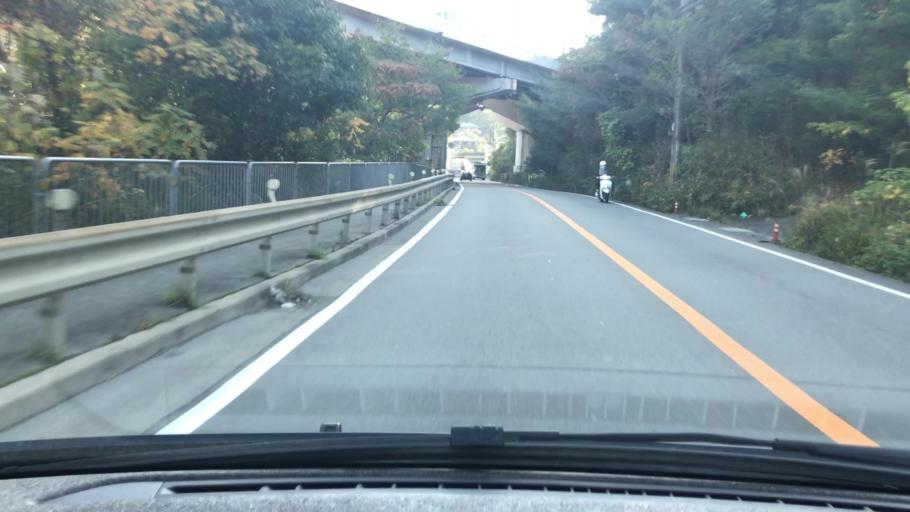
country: JP
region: Hyogo
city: Sandacho
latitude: 34.8338
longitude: 135.2800
